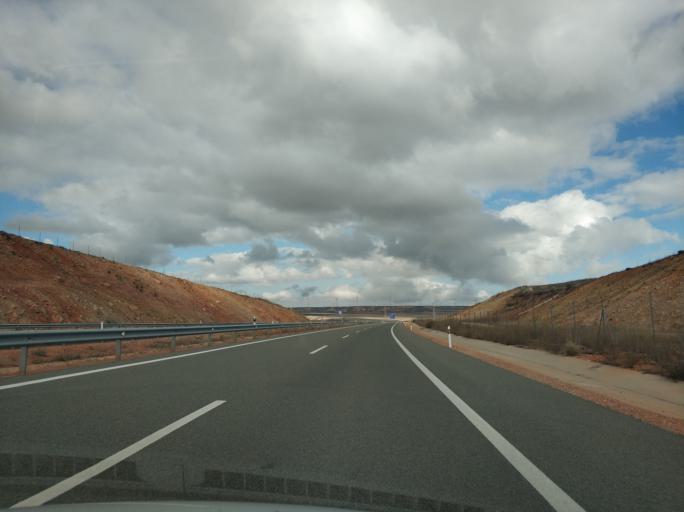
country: ES
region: Castille and Leon
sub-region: Provincia de Soria
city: Yelo
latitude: 41.2423
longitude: -2.4781
